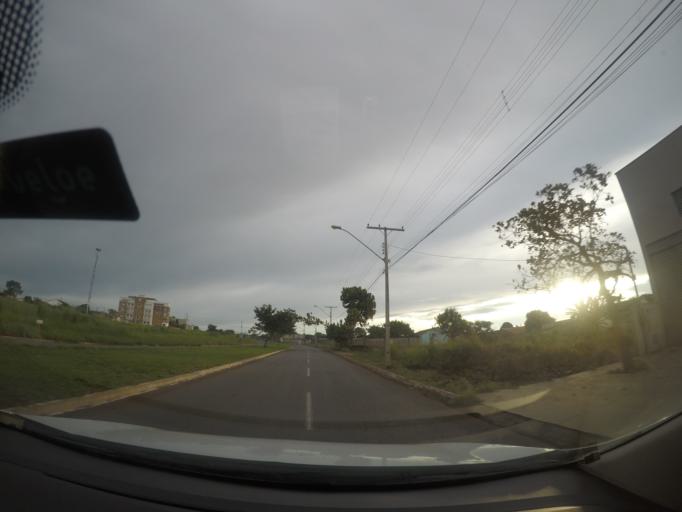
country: BR
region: Goias
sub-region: Goiania
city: Goiania
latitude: -16.7462
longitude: -49.3183
